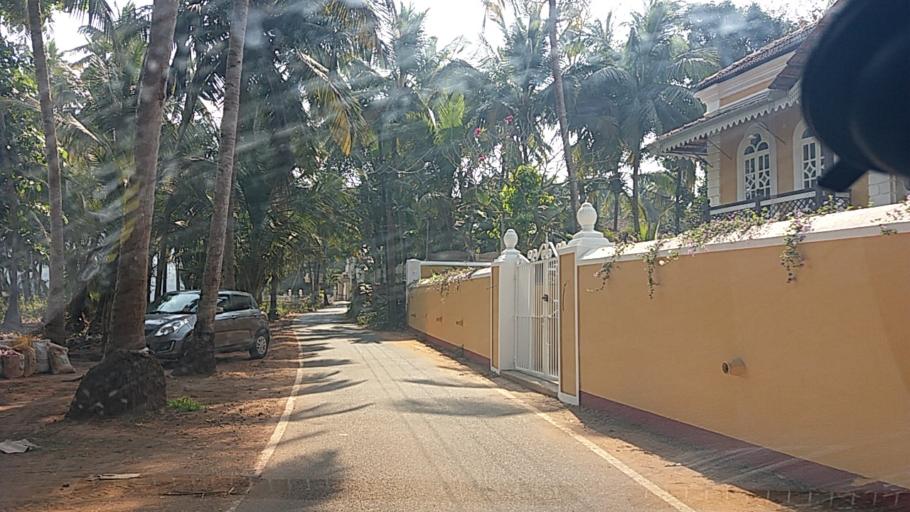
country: IN
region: Goa
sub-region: South Goa
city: Sancoale
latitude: 15.3603
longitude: 73.8881
